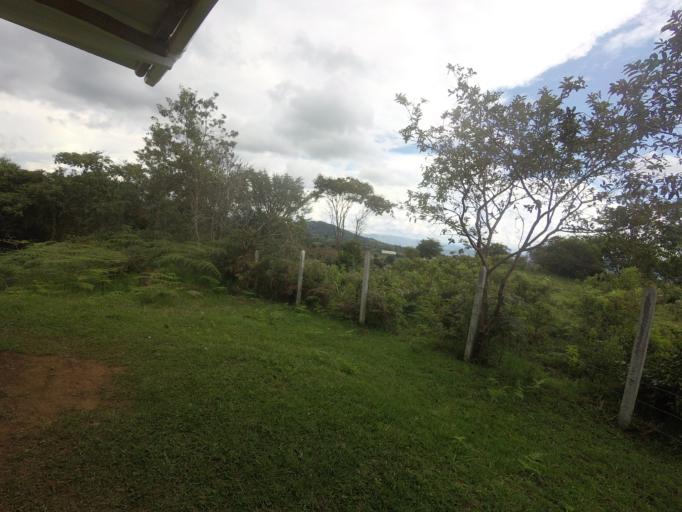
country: CO
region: Huila
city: Isnos
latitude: 1.9143
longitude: -76.2411
